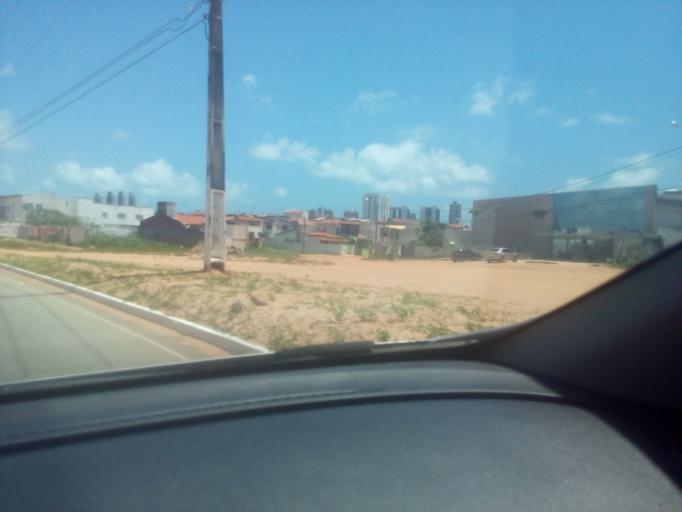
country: BR
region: Rio Grande do Norte
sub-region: Parnamirim
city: Parnamirim
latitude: -5.8936
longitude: -35.1931
